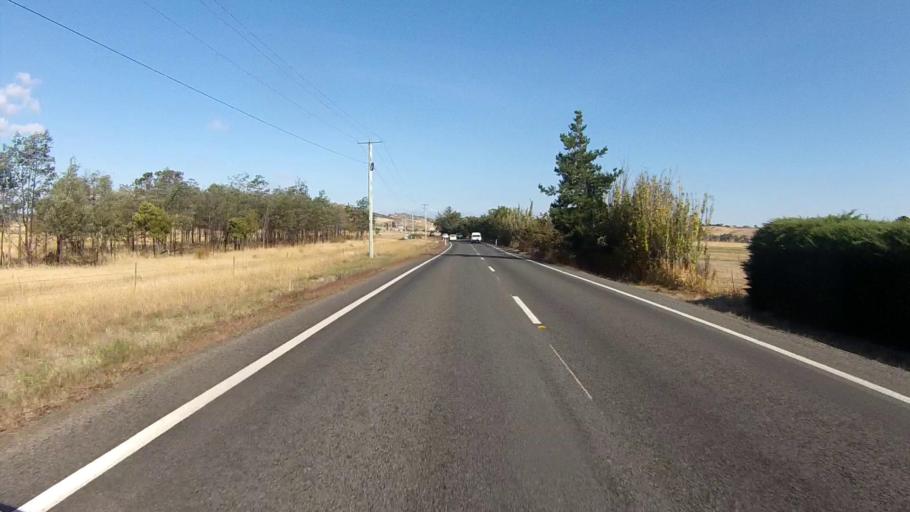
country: AU
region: Tasmania
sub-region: Sorell
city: Sorell
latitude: -42.7422
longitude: 147.5337
